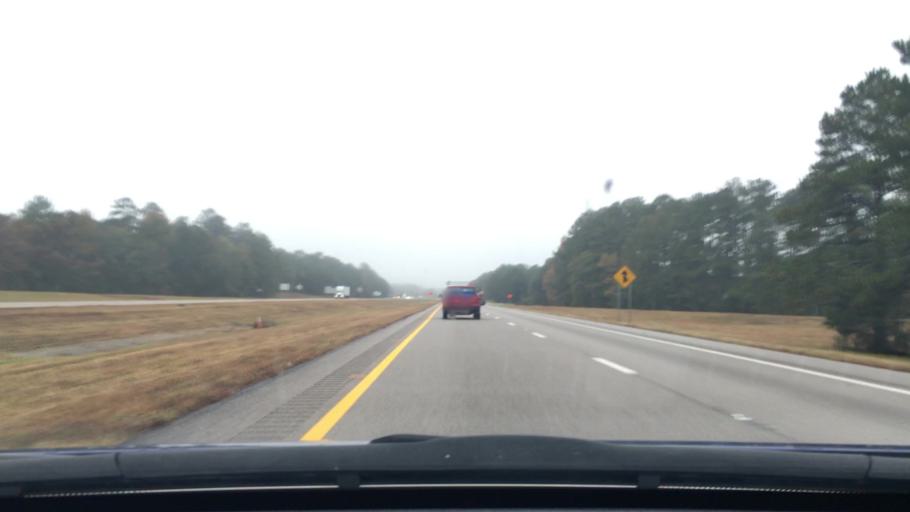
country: US
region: South Carolina
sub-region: Kershaw County
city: Camden
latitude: 34.2164
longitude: -80.5315
